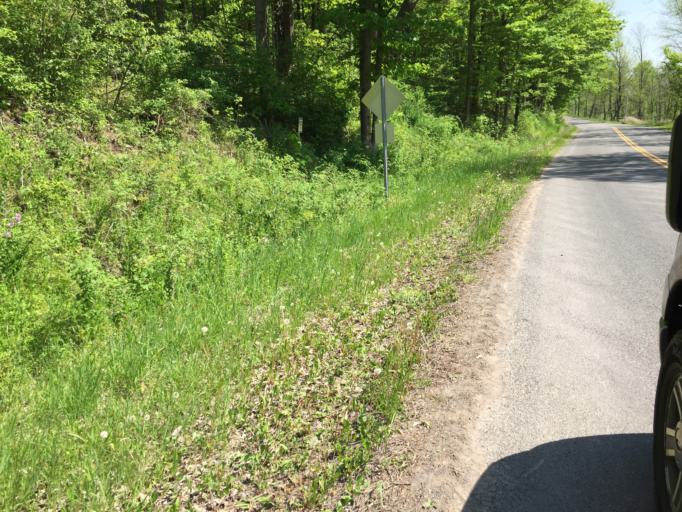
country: US
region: New York
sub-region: Wayne County
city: Marion
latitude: 43.1259
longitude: -77.1730
